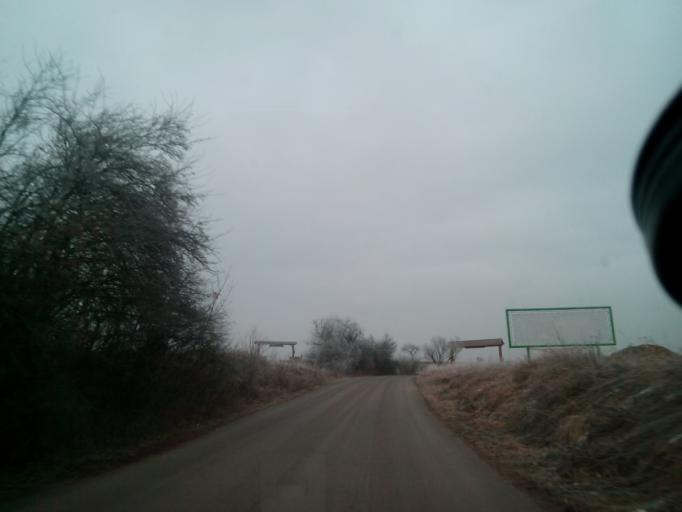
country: SK
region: Presovsky
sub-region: Okres Poprad
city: Poprad
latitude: 48.9666
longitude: 20.3858
